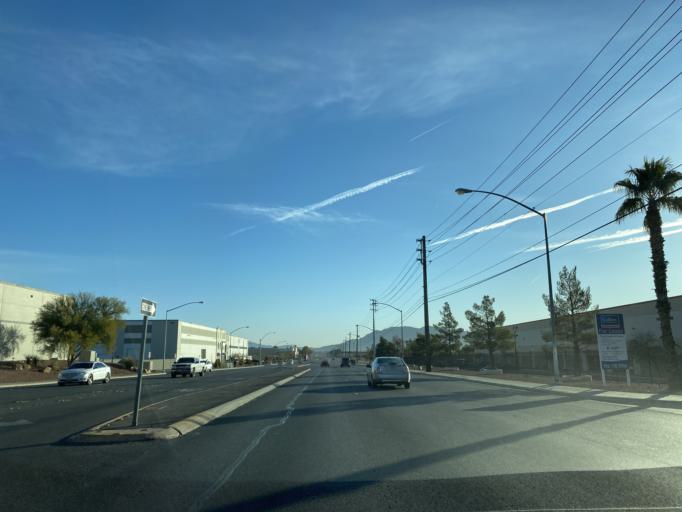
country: US
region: Nevada
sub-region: Clark County
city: Nellis Air Force Base
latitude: 36.2403
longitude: -115.0775
